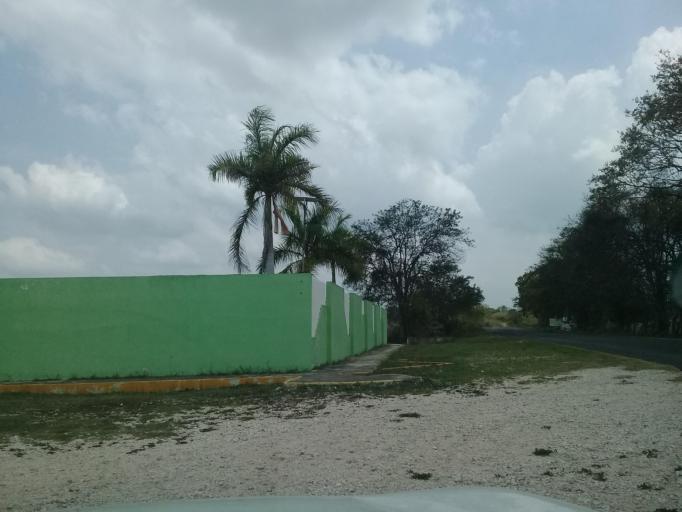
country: MX
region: Veracruz
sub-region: Emiliano Zapata
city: Plan del Rio
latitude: 19.3528
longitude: -96.6585
